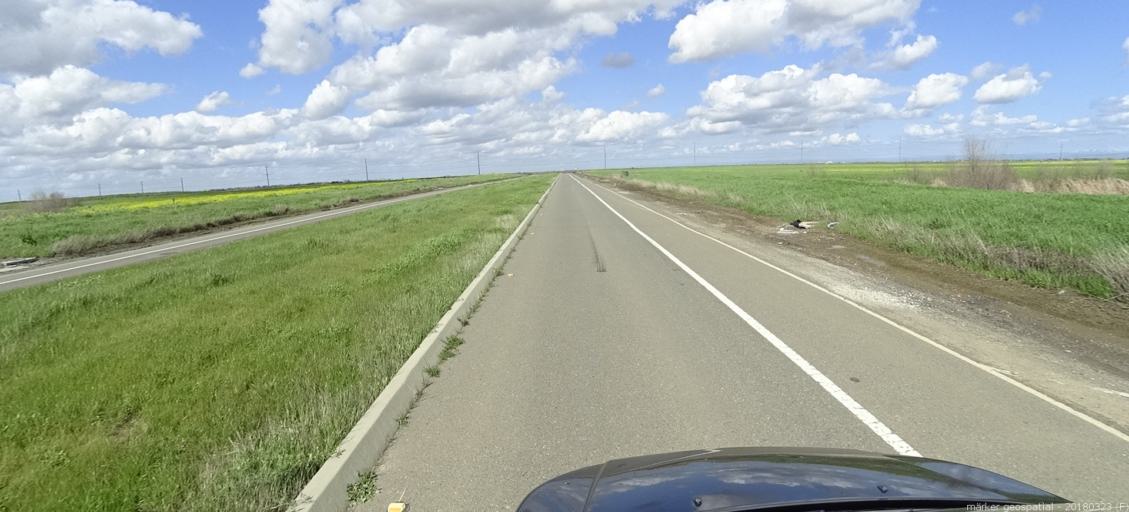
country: US
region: California
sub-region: Sacramento County
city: Elverta
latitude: 38.7104
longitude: -121.5641
